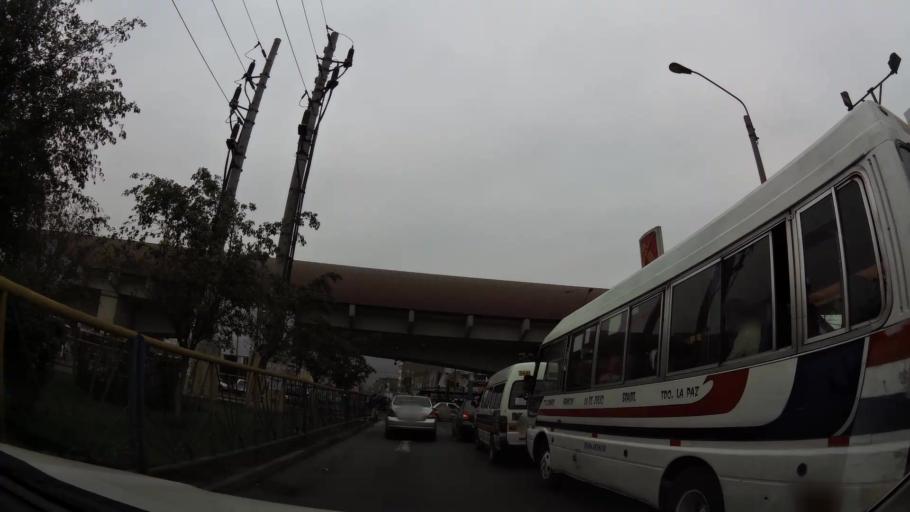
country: PE
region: Lima
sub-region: Lima
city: Independencia
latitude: -11.9848
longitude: -77.0073
